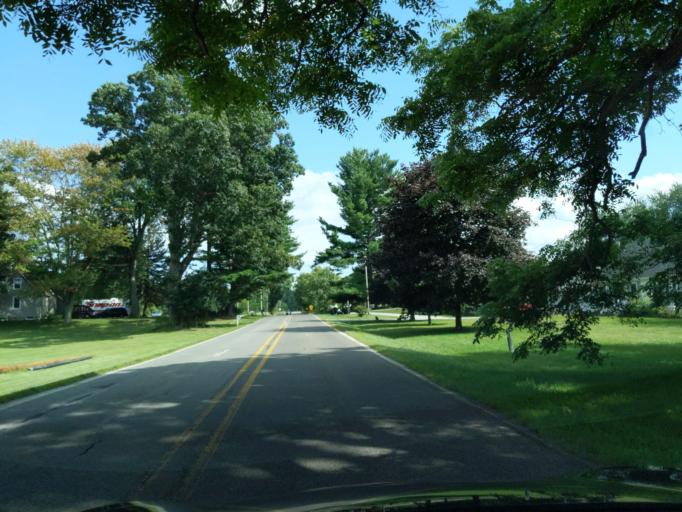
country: US
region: Michigan
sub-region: Jackson County
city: Jackson
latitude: 42.2881
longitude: -84.4667
